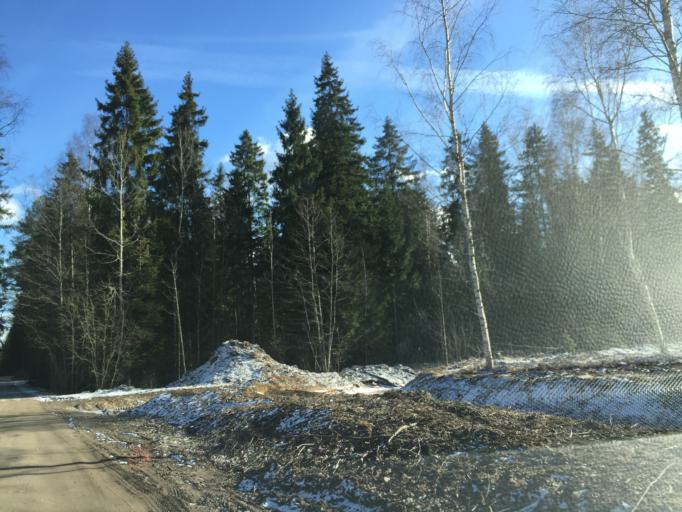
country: LV
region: Garkalne
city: Garkalne
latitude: 56.9469
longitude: 24.4548
